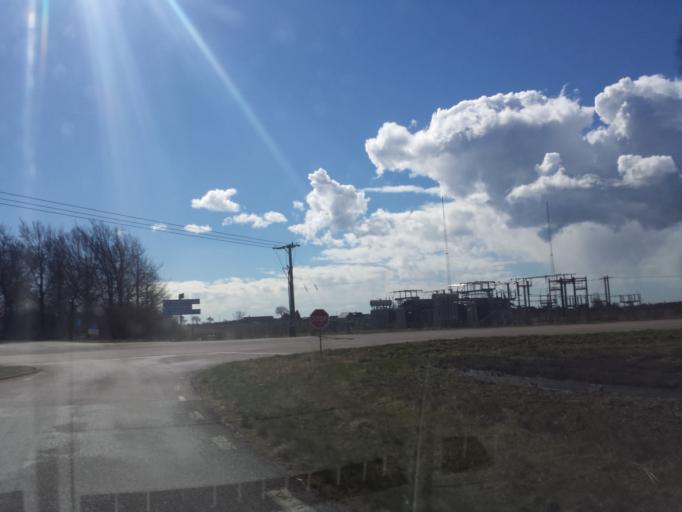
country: SE
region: Skane
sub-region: Ystads Kommun
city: Kopingebro
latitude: 55.4668
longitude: 13.9310
